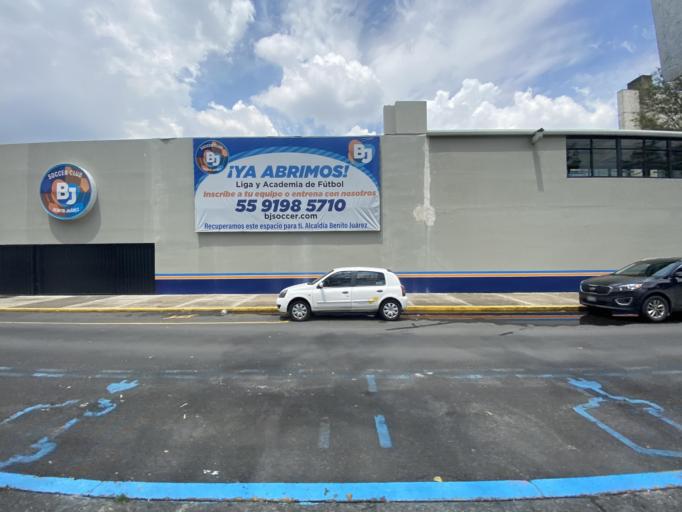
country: MX
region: Mexico City
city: Coyoacan
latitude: 19.3581
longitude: -99.1557
